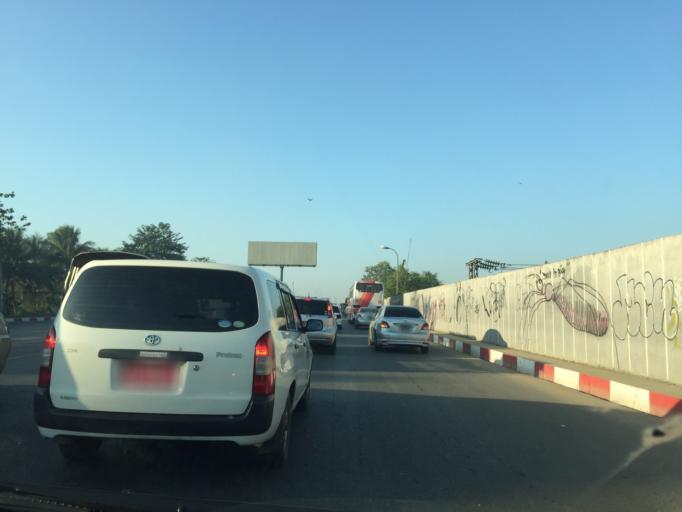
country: MM
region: Yangon
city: Yangon
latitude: 16.8655
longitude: 96.1814
